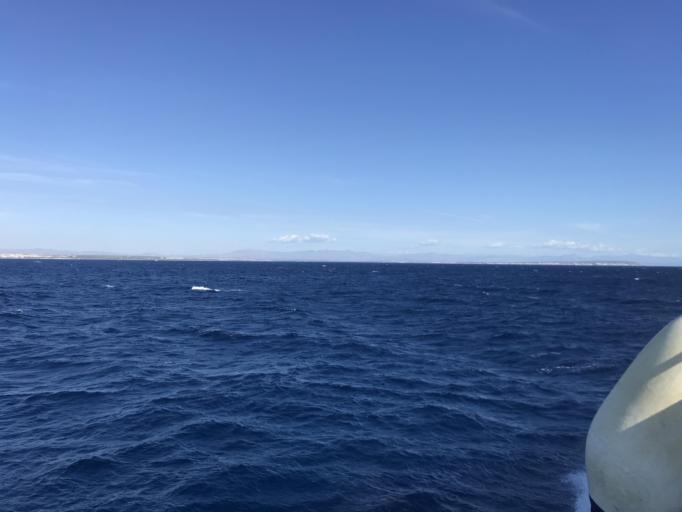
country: ES
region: Valencia
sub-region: Provincia de Alicante
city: Guardamar del Segura
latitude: 38.0495
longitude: -0.5996
